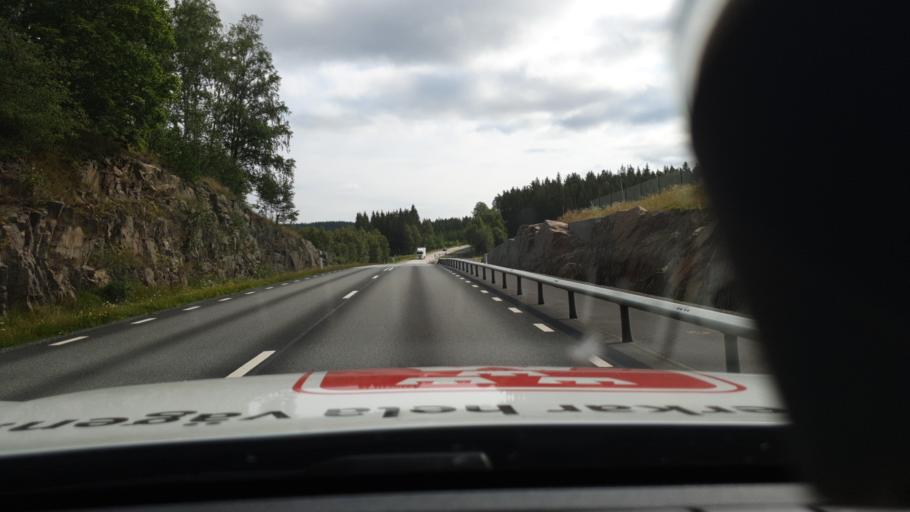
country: SE
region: Joenkoeping
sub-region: Jonkopings Kommun
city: Huskvarna
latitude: 57.7786
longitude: 14.3417
